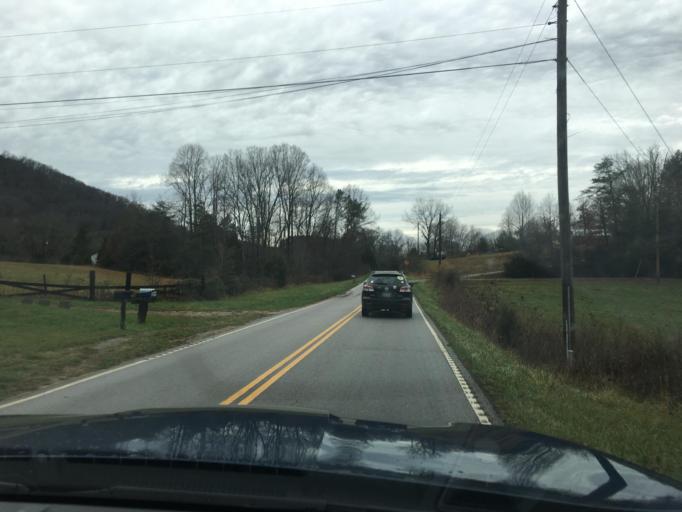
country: US
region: Tennessee
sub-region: McMinn County
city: Englewood
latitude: 35.3467
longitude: -84.3980
